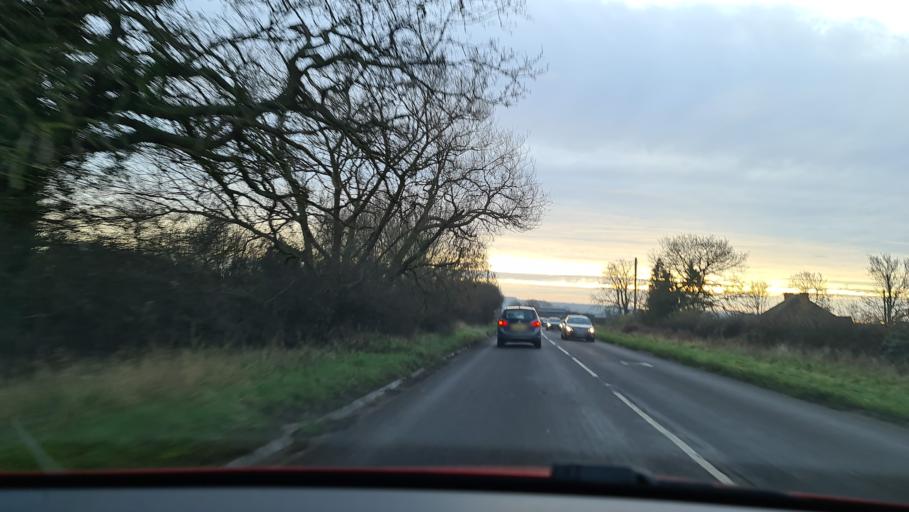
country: GB
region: England
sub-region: Buckinghamshire
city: Princes Risborough
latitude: 51.7499
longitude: -0.8776
